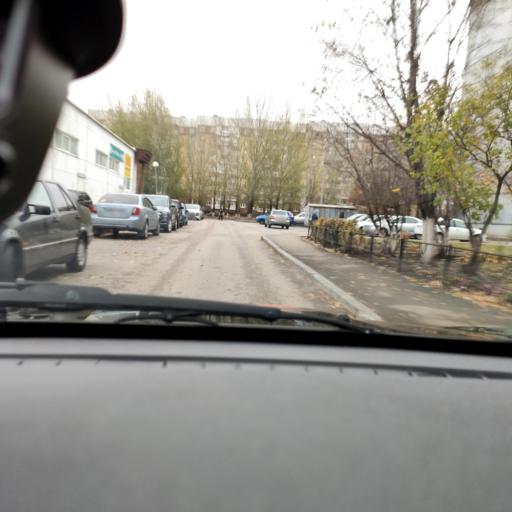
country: RU
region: Samara
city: Tol'yatti
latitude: 53.5395
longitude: 49.3434
